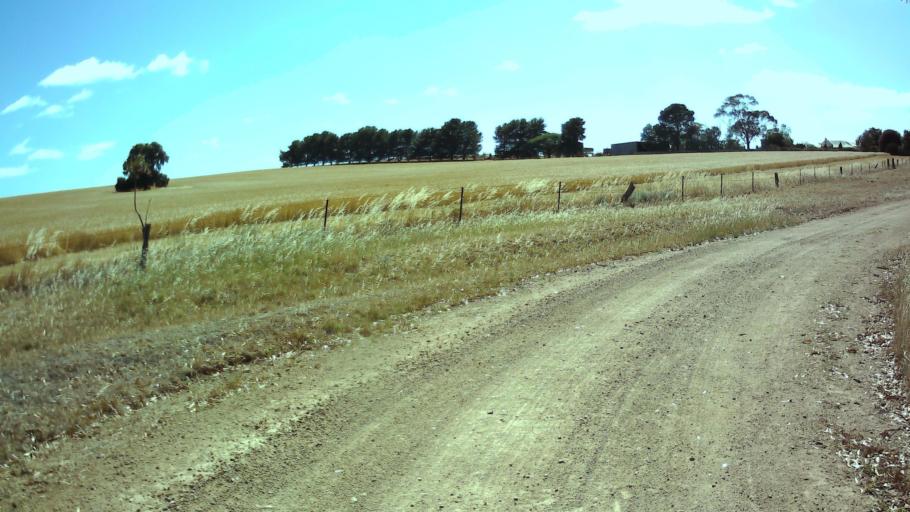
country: AU
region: New South Wales
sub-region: Weddin
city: Grenfell
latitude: -33.9648
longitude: 148.4117
